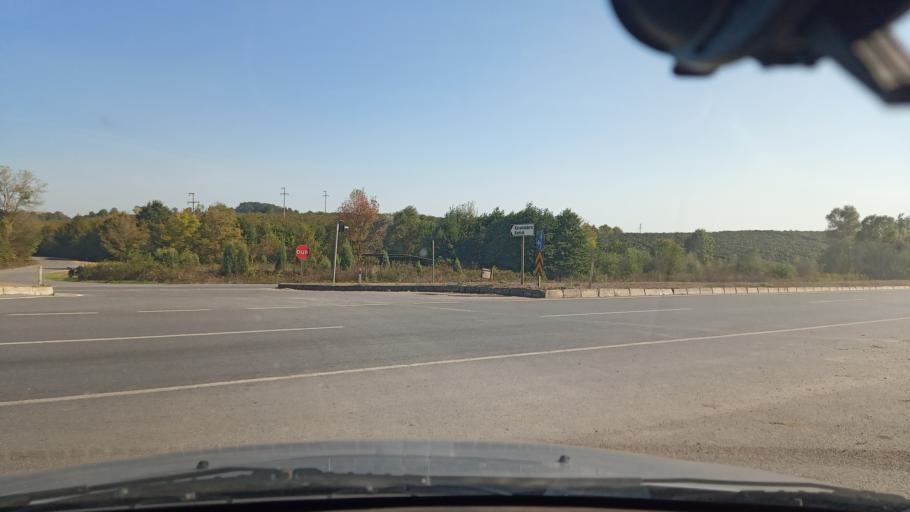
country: TR
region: Sakarya
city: Karasu
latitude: 41.0543
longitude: 30.6351
